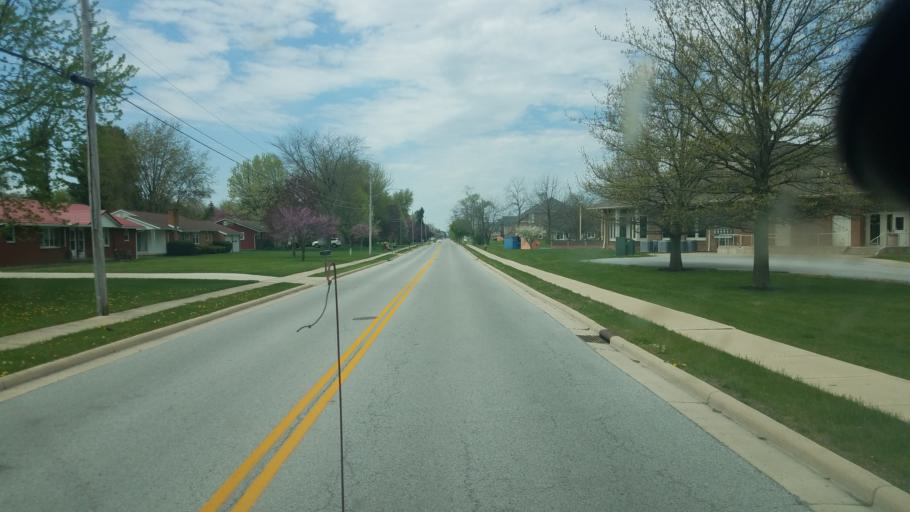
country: US
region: Ohio
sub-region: Hardin County
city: Ada
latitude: 40.7622
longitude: -83.8287
